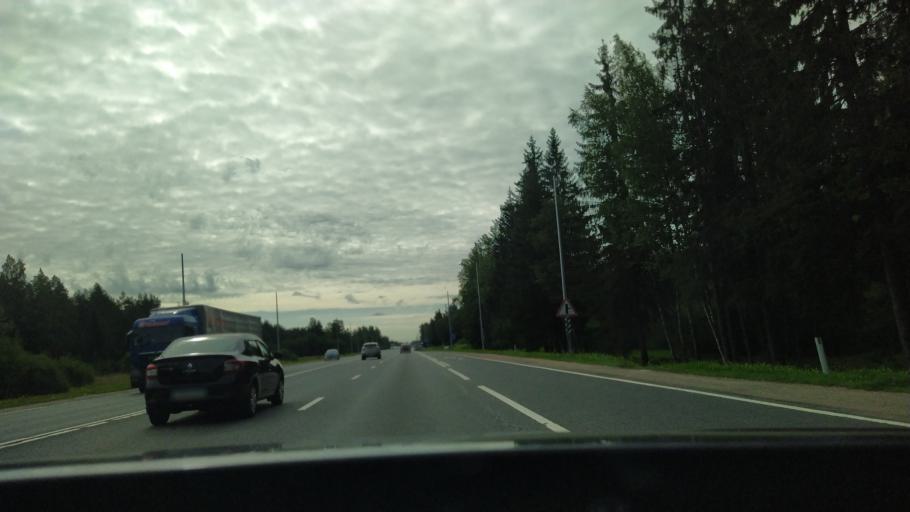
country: RU
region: Leningrad
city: Ul'yanovka
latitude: 59.5807
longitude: 30.8048
